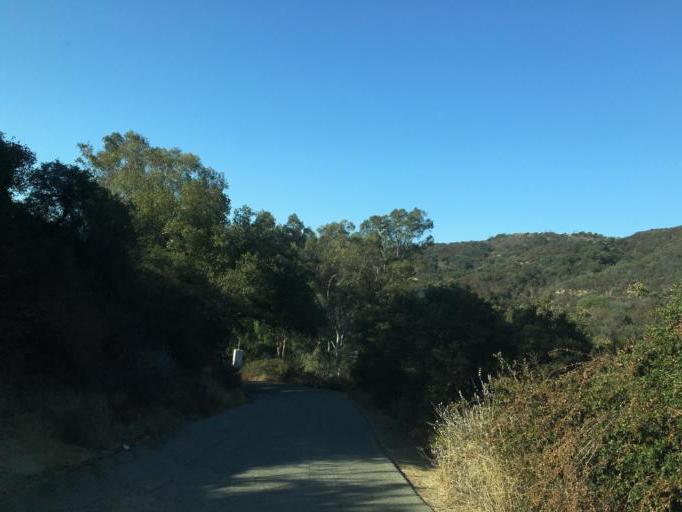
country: US
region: California
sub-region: Los Angeles County
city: Topanga
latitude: 34.1155
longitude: -118.5907
